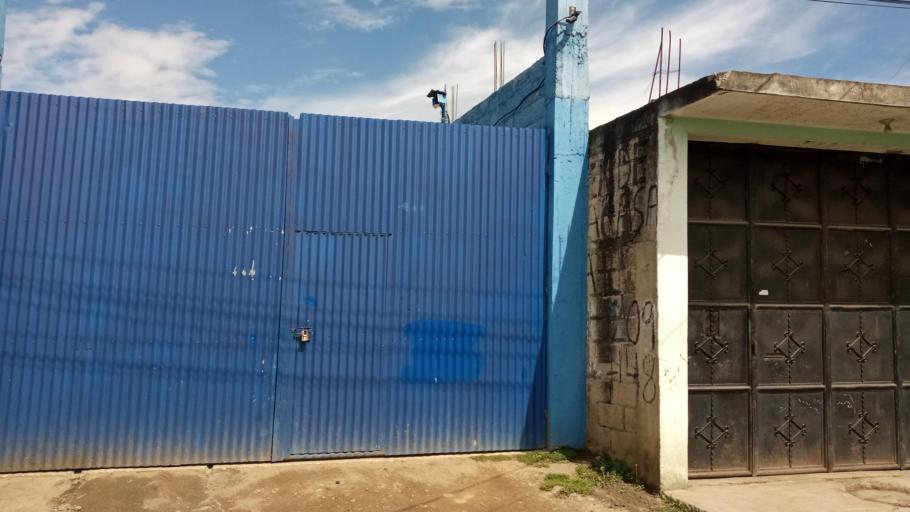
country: GT
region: Quetzaltenango
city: Quetzaltenango
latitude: 14.8426
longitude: -91.5092
